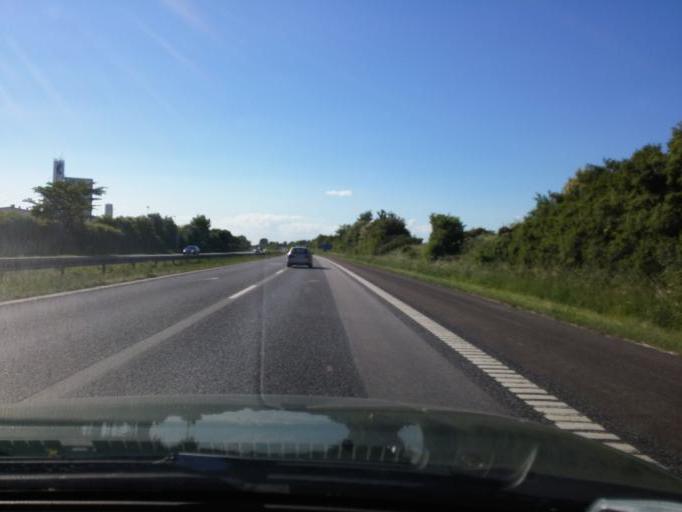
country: DK
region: South Denmark
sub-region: Middelfart Kommune
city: Ejby
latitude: 55.4491
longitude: 9.9587
